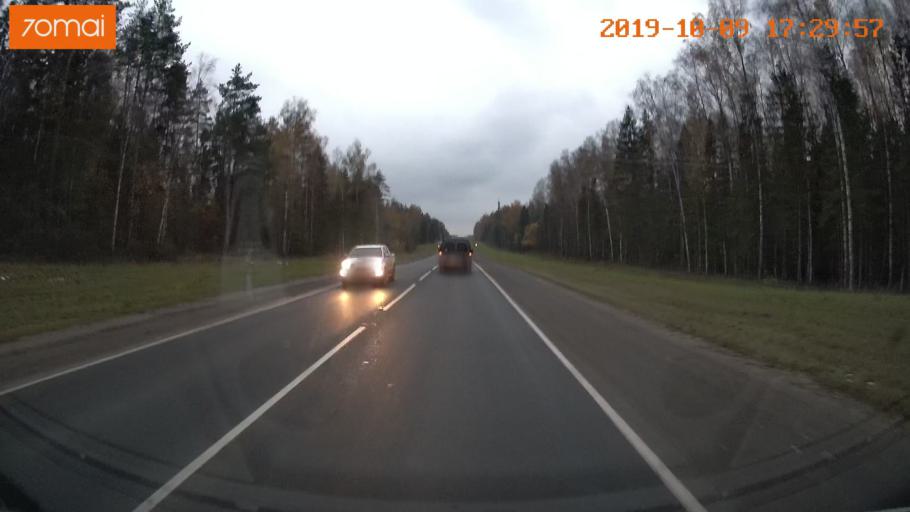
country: RU
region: Ivanovo
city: Bogorodskoye
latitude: 57.1462
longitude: 41.0542
